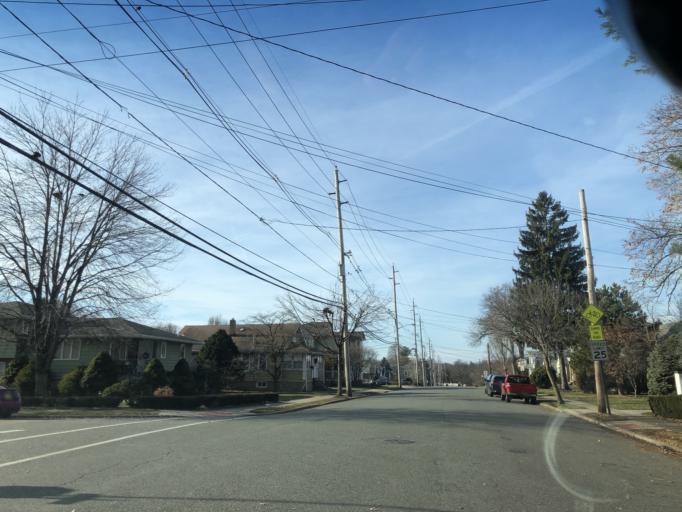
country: US
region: New Jersey
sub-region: Bergen County
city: Fair Lawn
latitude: 40.9309
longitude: -74.1325
